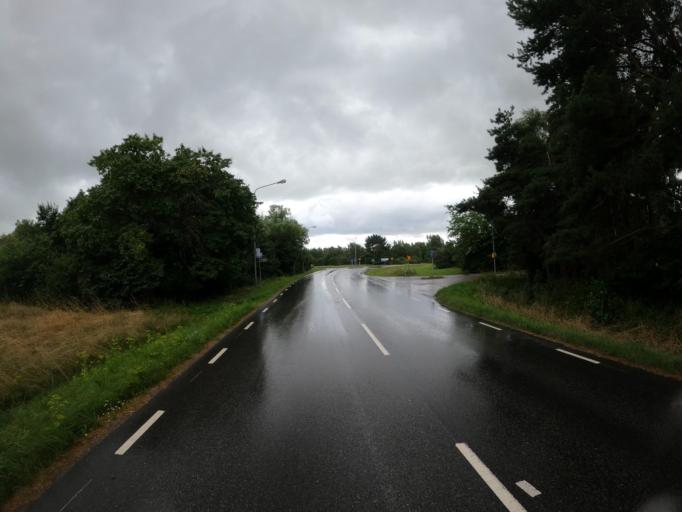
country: SE
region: Skane
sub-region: Hoors Kommun
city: Loberod
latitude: 55.7235
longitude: 13.4651
